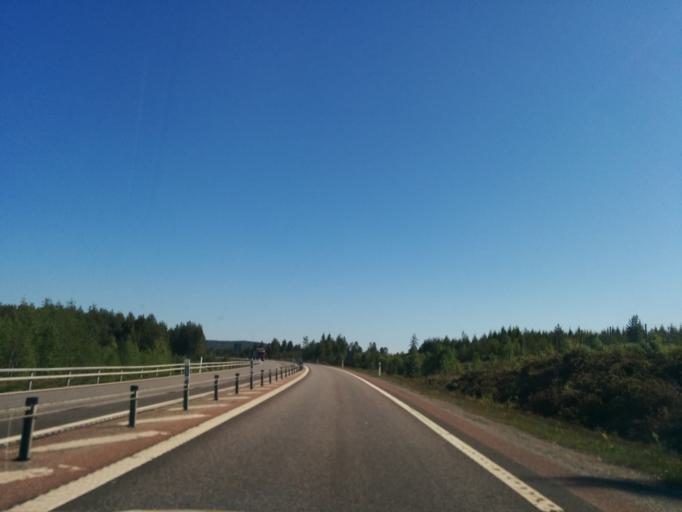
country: SE
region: Vaesternorrland
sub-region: Haernoesands Kommun
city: Haernoesand
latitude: 62.7226
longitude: 17.9211
